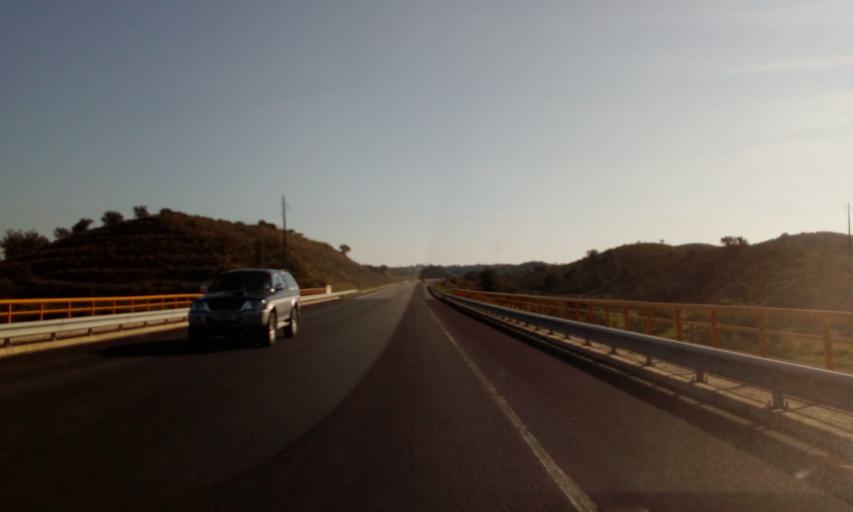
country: PT
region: Faro
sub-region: Castro Marim
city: Castro Marim
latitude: 37.2532
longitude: -7.4786
